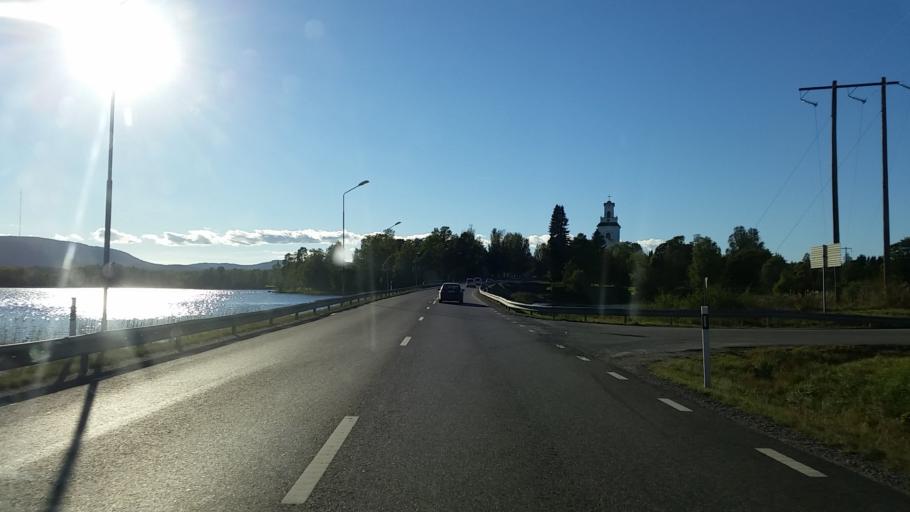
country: SE
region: Gaevleborg
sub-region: Hudiksvalls Kommun
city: Sorforsa
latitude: 61.7337
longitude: 16.9461
